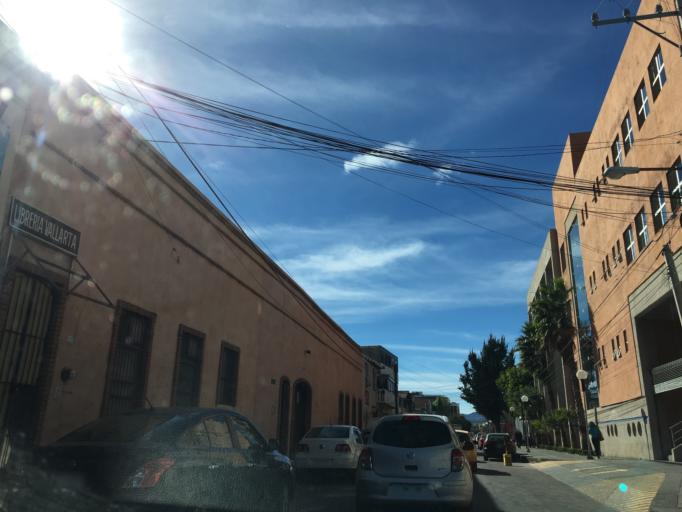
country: MX
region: San Luis Potosi
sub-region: San Luis Potosi
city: San Luis Potosi
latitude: 22.1490
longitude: -100.9837
